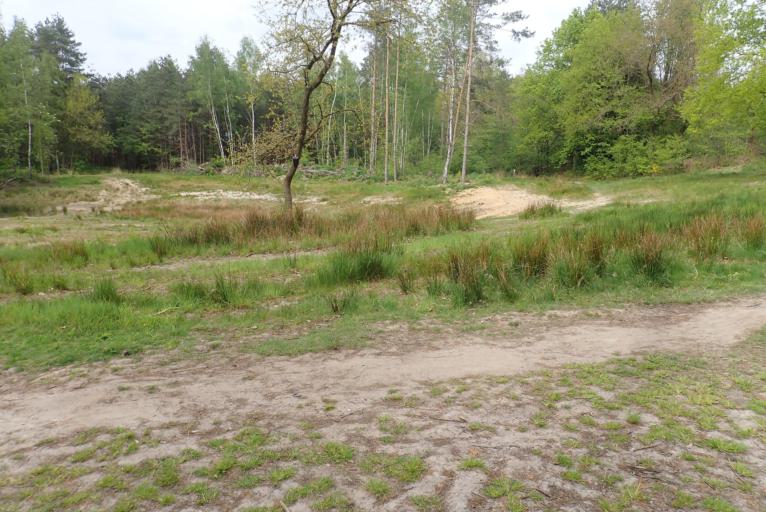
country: BE
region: Flanders
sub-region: Provincie Antwerpen
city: Vosselaar
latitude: 51.3241
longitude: 4.8864
